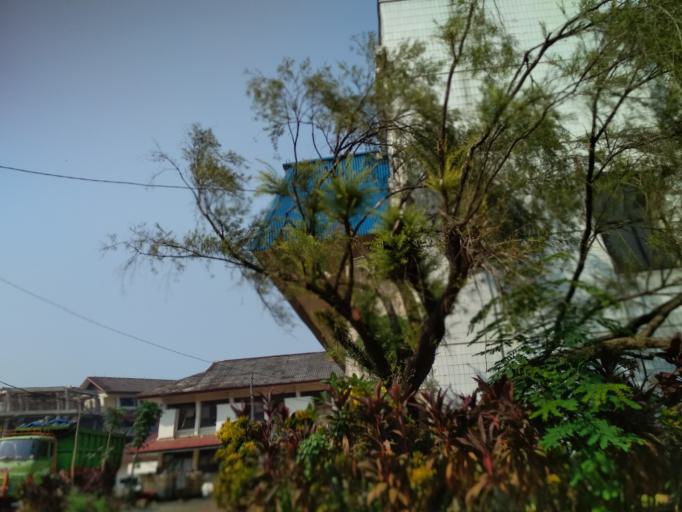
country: ID
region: West Java
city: Ciampea
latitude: -6.5563
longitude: 106.7247
